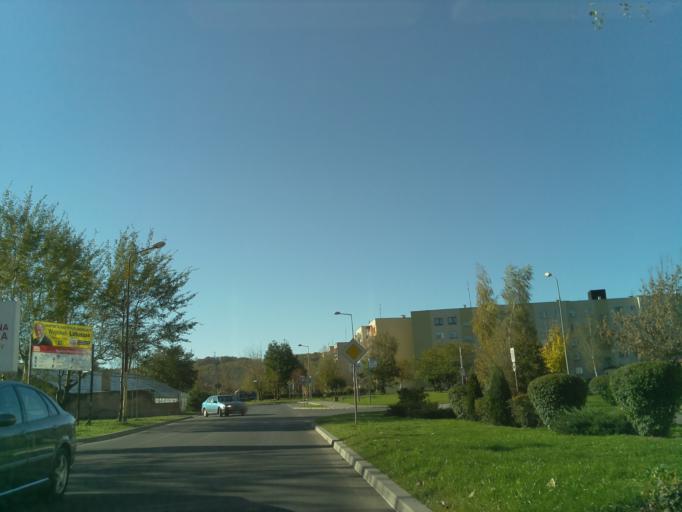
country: PL
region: Lower Silesian Voivodeship
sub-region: Powiat swidnicki
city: Swiebodzice
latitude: 50.8641
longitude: 16.3178
